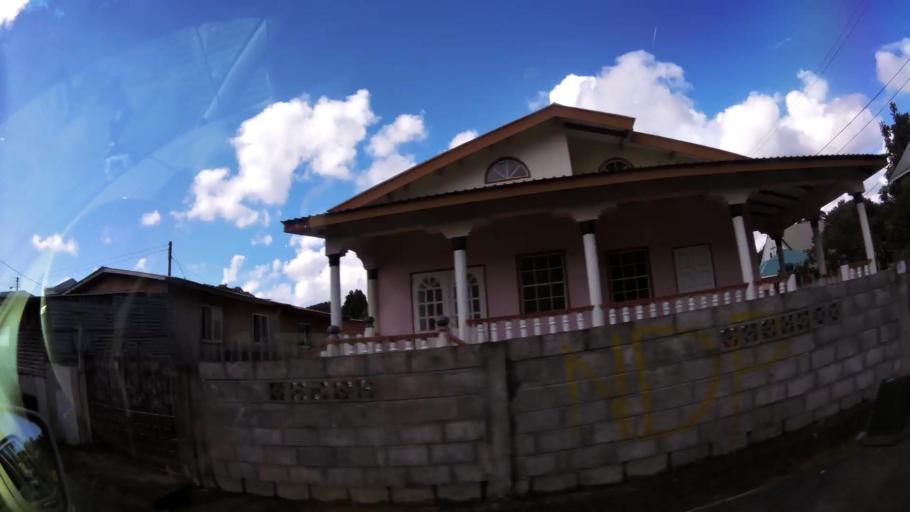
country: VC
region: Saint George
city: Kingstown
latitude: 13.1319
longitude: -61.1936
